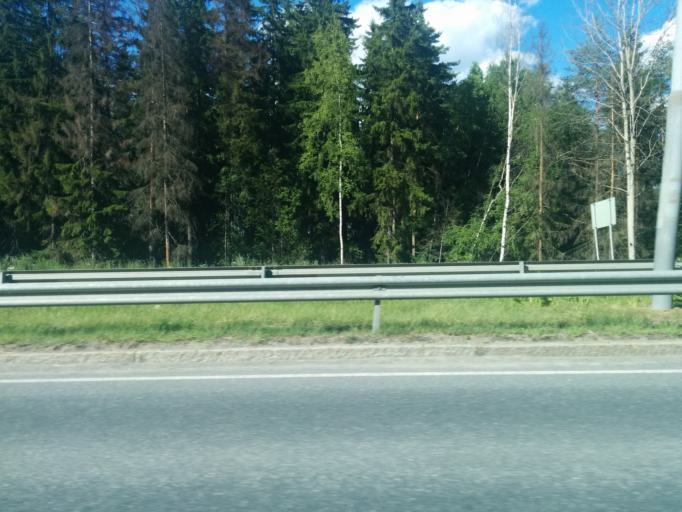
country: FI
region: Pirkanmaa
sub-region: Tampere
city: Tampere
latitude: 61.5006
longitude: 23.8732
